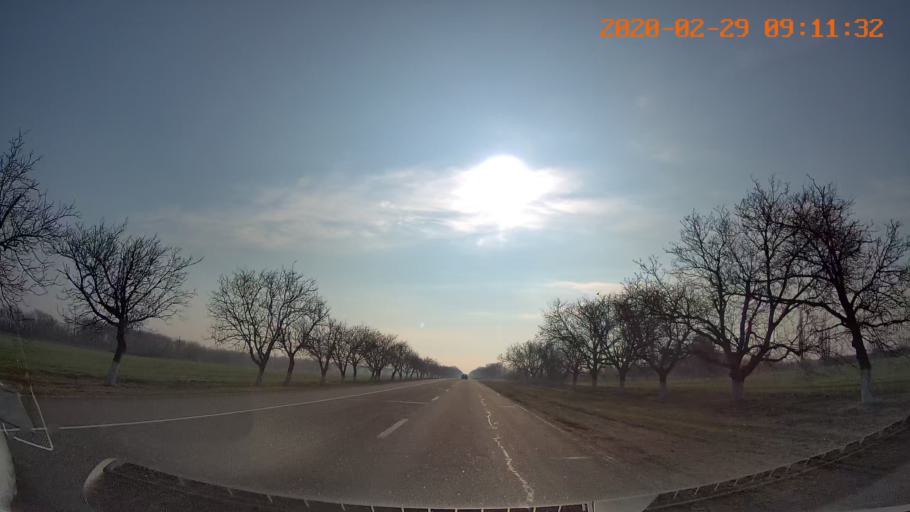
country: MD
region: Telenesti
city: Slobozia
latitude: 46.8342
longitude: 29.8017
